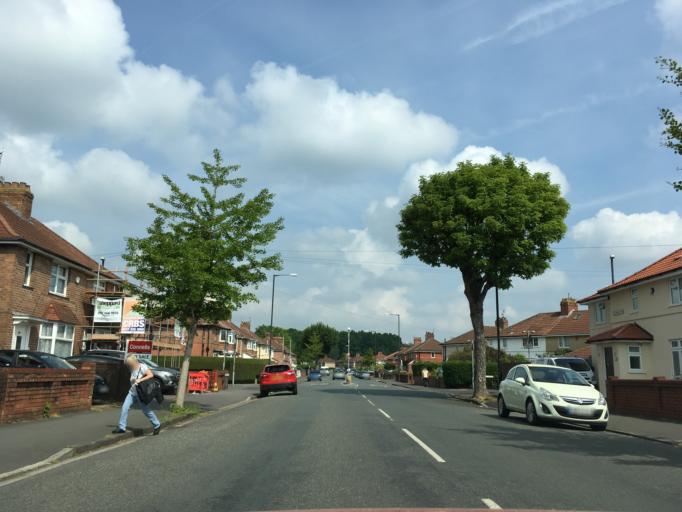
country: GB
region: England
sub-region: Bristol
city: Bristol
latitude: 51.4386
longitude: -2.6153
